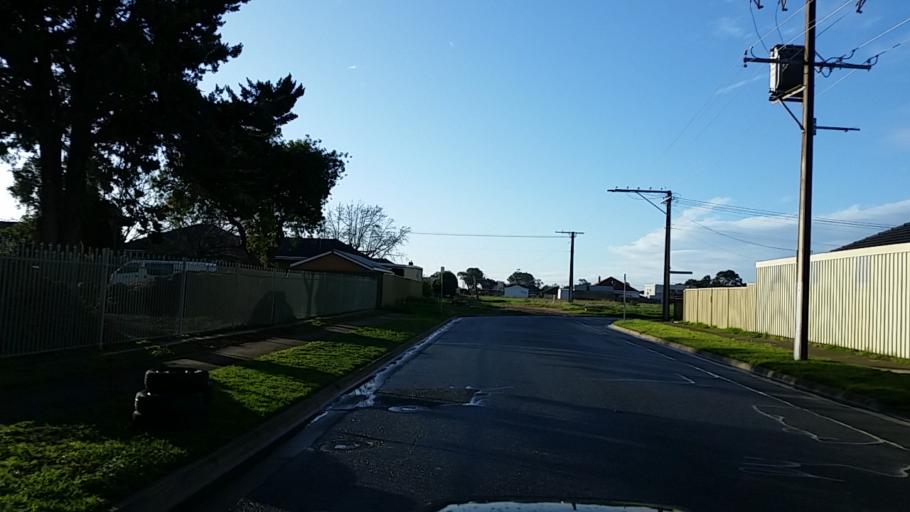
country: AU
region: South Australia
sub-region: Charles Sturt
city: Findon
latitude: -34.9038
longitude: 138.5347
